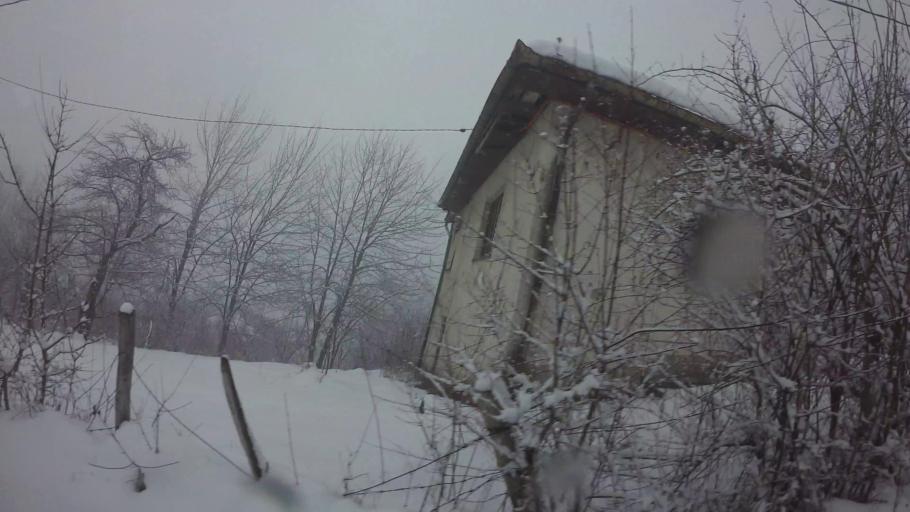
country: BA
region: Federation of Bosnia and Herzegovina
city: Kobilja Glava
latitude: 43.8463
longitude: 18.4225
